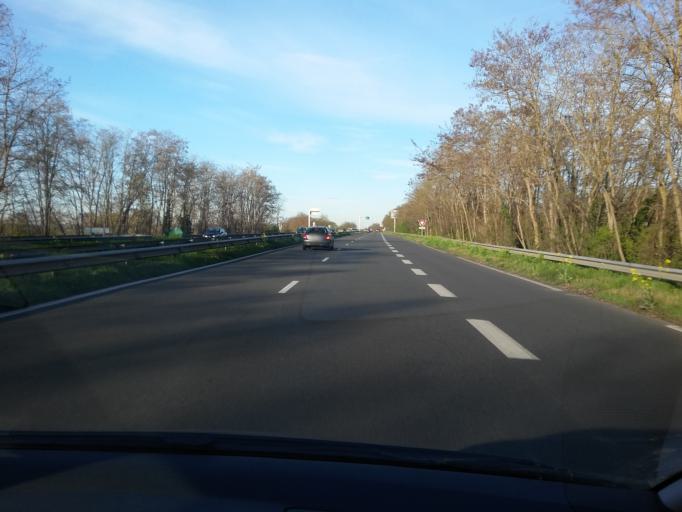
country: FR
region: Picardie
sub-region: Departement de l'Oise
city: Lacroix-Saint-Ouen
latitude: 49.3617
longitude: 2.7691
